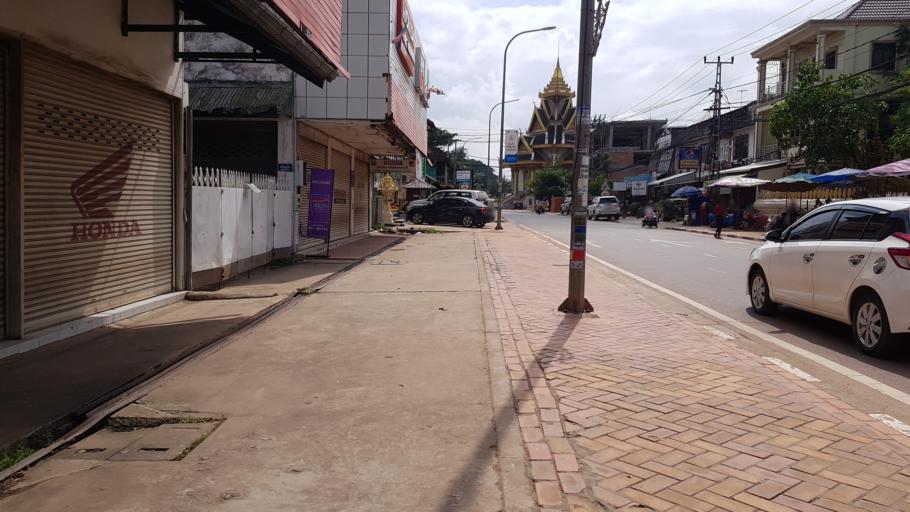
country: LA
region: Vientiane
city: Vientiane
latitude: 17.9596
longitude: 102.6147
